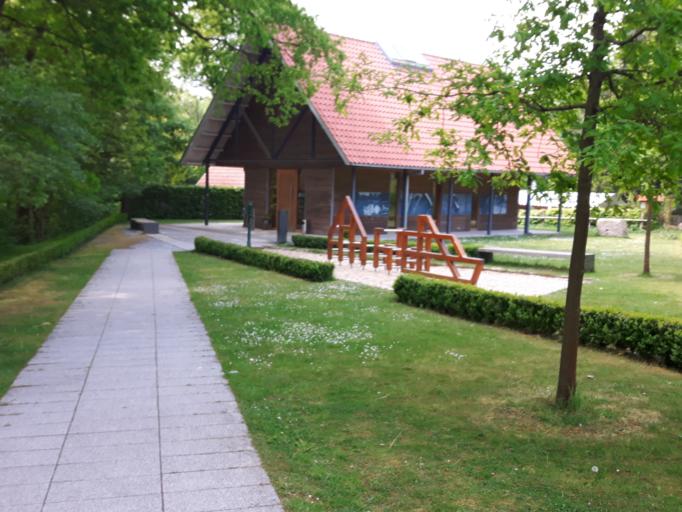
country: DE
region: North Rhine-Westphalia
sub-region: Regierungsbezirk Detmold
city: Hovelhof
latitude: 51.8541
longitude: 8.6892
